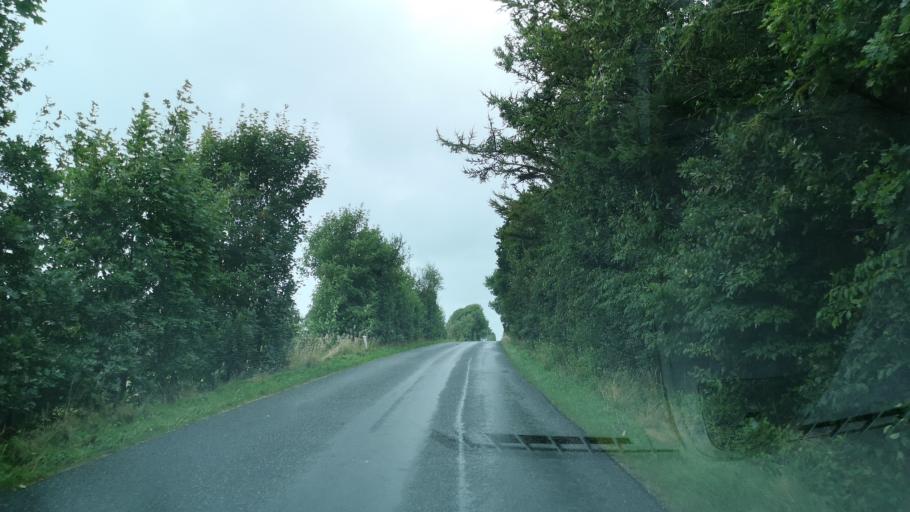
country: DK
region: Central Jutland
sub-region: Ringkobing-Skjern Kommune
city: Videbaek
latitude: 56.0591
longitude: 8.6765
